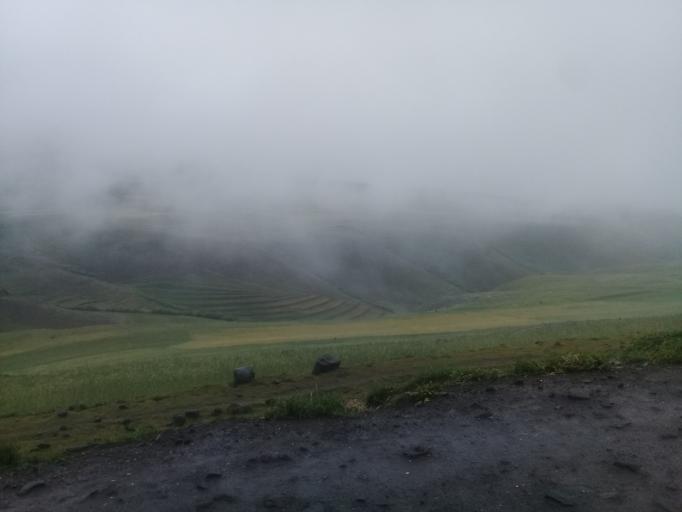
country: LS
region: Mokhotlong
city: Mokhotlong
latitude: -29.3800
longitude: 28.9824
